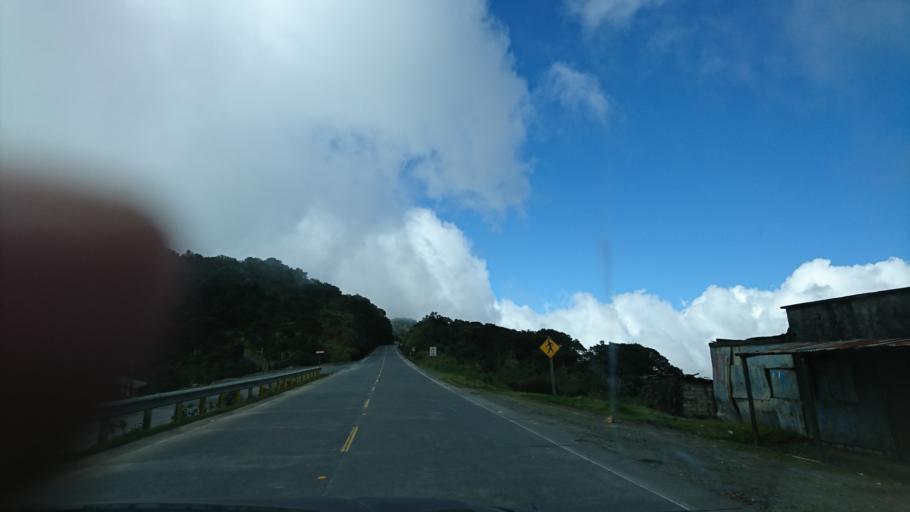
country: BO
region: La Paz
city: Coroico
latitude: -16.2871
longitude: -67.8496
